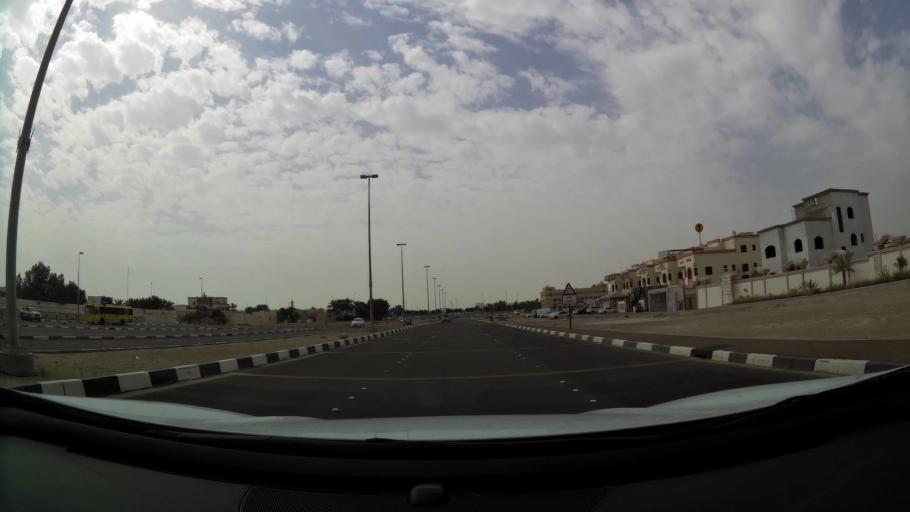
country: AE
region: Abu Dhabi
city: Abu Dhabi
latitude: 24.2983
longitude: 54.6314
